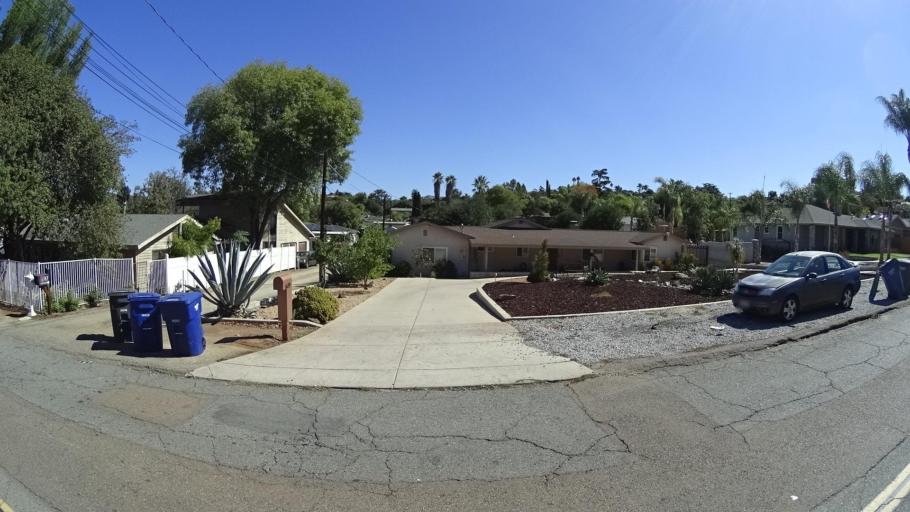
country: US
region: California
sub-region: San Diego County
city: Winter Gardens
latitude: 32.8194
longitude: -116.9303
